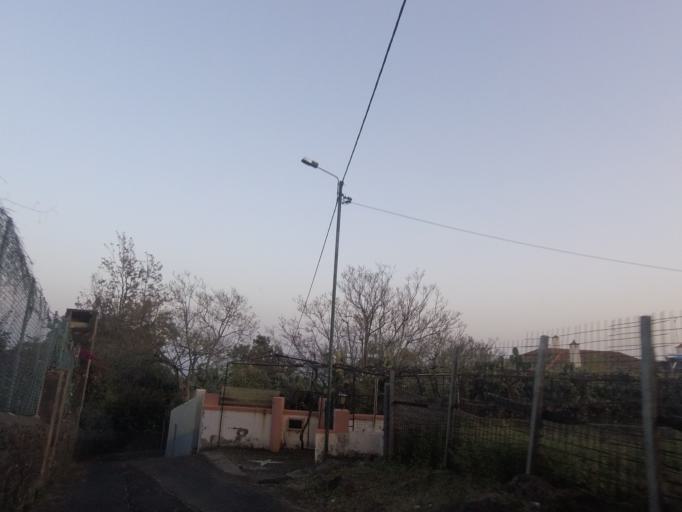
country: PT
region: Madeira
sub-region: Funchal
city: Funchal
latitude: 32.6438
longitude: -16.9280
